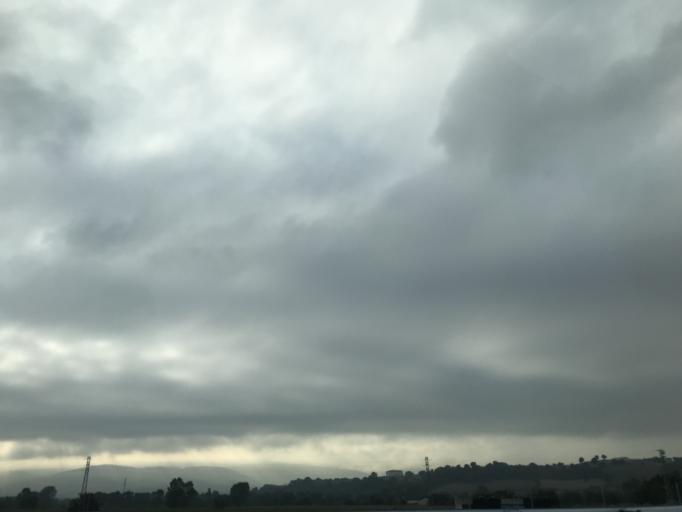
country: TR
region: Balikesir
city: Susurluk
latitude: 39.9236
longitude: 28.1330
